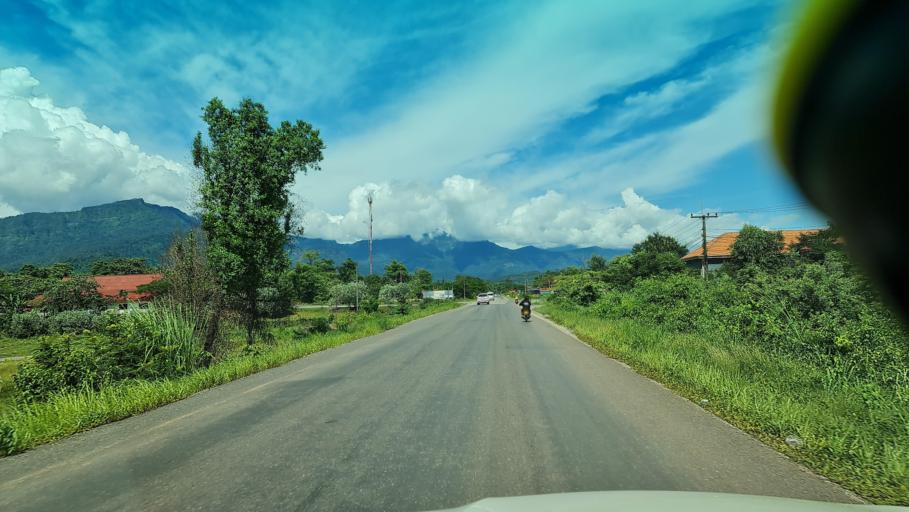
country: LA
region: Bolikhamxai
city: Ban Nahin
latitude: 18.3004
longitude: 104.1175
